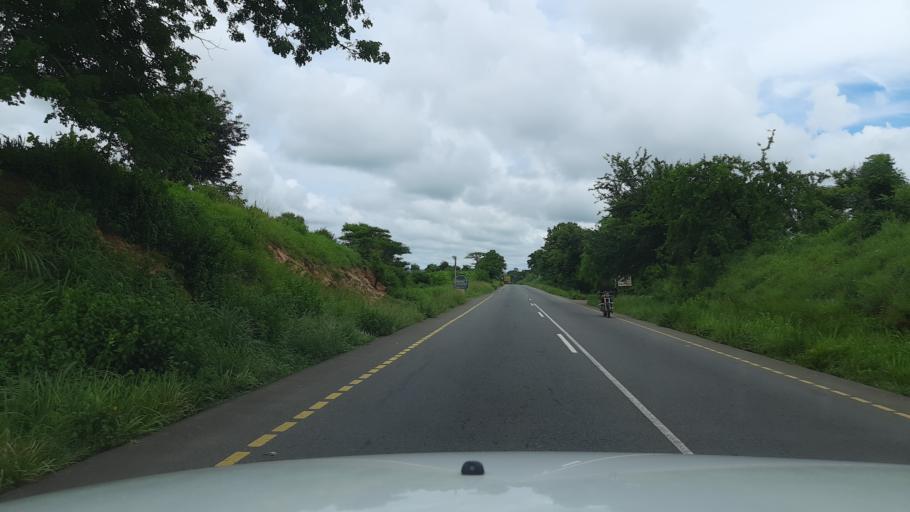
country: TZ
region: Pwani
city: Lugoba
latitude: -5.9642
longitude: 38.2236
